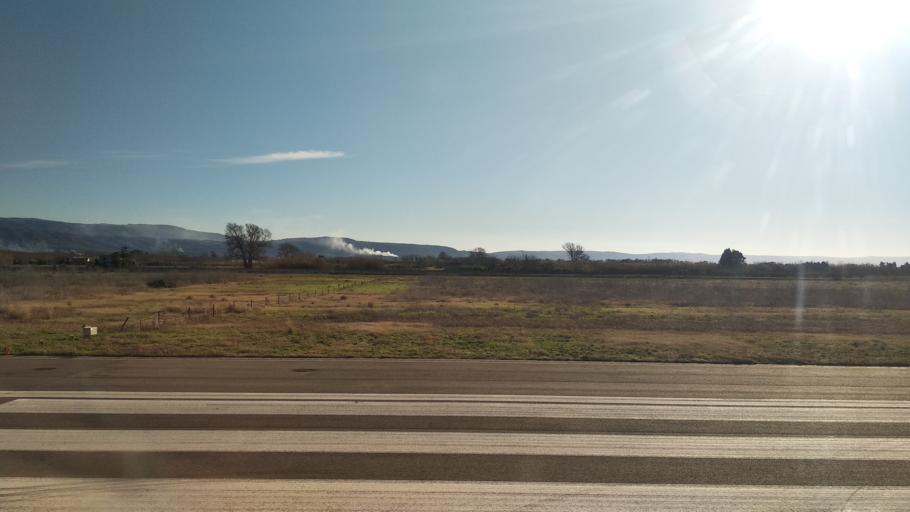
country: IT
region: Calabria
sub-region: Provincia di Catanzaro
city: Santa Eufemia Lamezia
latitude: 38.9034
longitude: 16.2586
